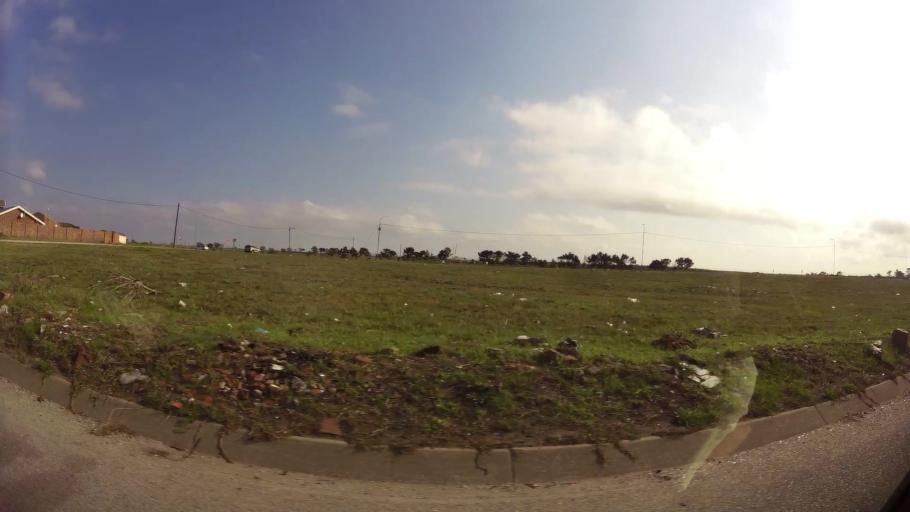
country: ZA
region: Eastern Cape
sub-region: Nelson Mandela Bay Metropolitan Municipality
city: Port Elizabeth
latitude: -33.9191
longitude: 25.5303
